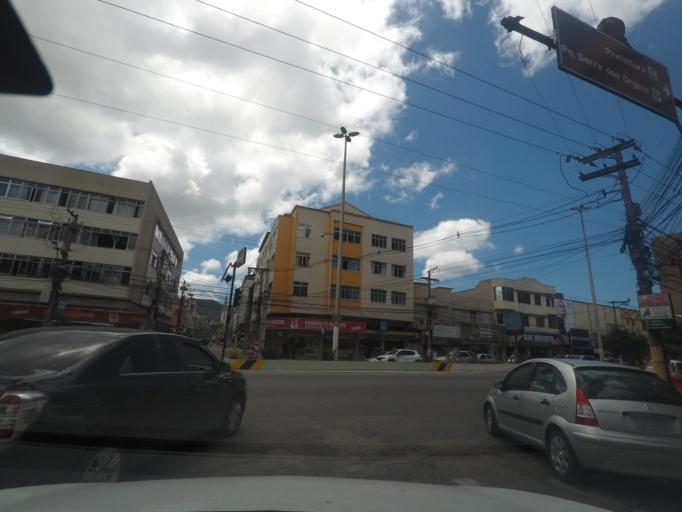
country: BR
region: Rio de Janeiro
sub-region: Teresopolis
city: Teresopolis
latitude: -22.4105
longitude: -42.9681
